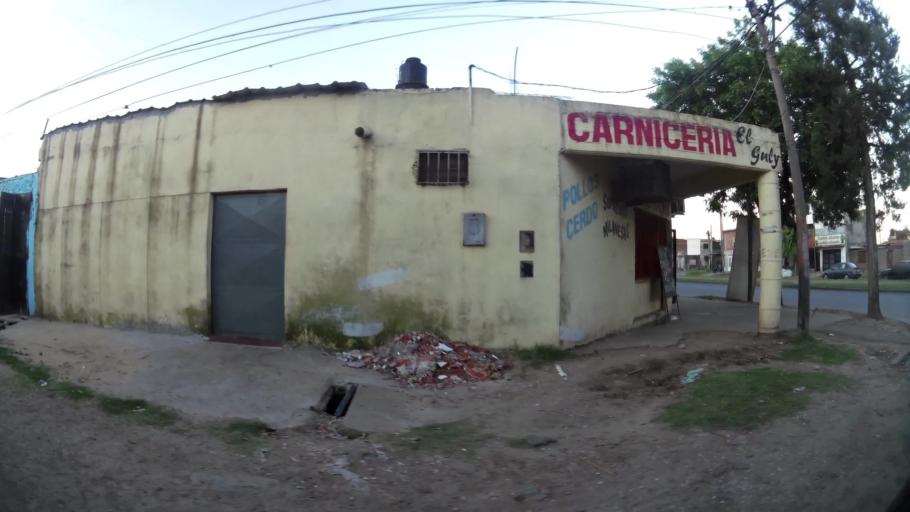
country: AR
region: Santa Fe
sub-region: Departamento de Rosario
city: Rosario
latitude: -32.9734
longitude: -60.6880
